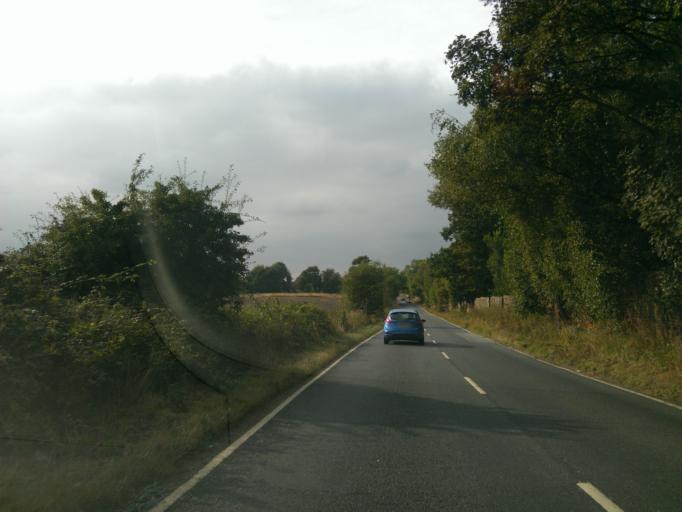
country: GB
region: England
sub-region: Essex
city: Great Totham
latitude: 51.8004
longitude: 0.6961
